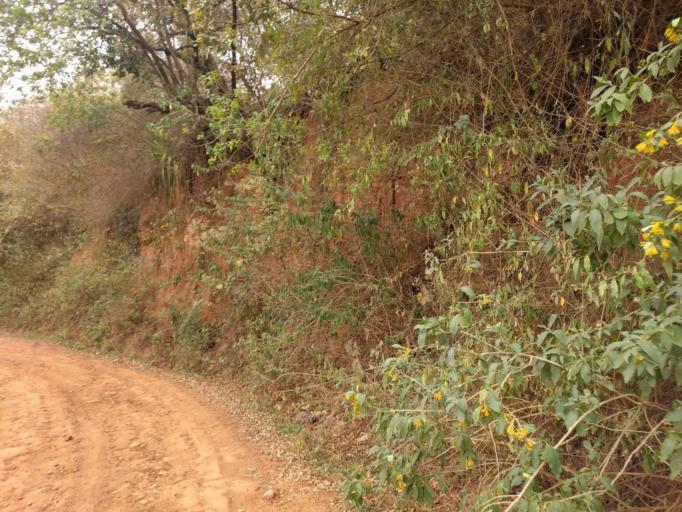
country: BO
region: Santa Cruz
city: Samaipata
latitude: -18.1867
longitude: -63.8785
